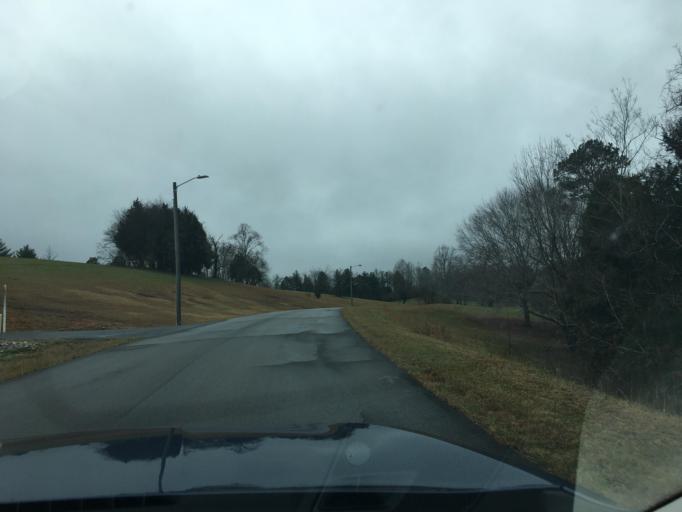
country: US
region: Tennessee
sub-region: McMinn County
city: Athens
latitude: 35.4561
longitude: -84.6382
